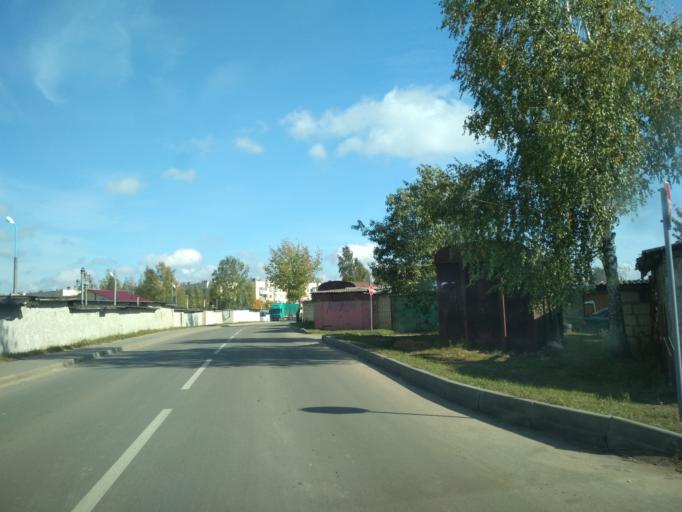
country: BY
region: Minsk
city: Mar''ina Horka
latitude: 53.5007
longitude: 28.1555
